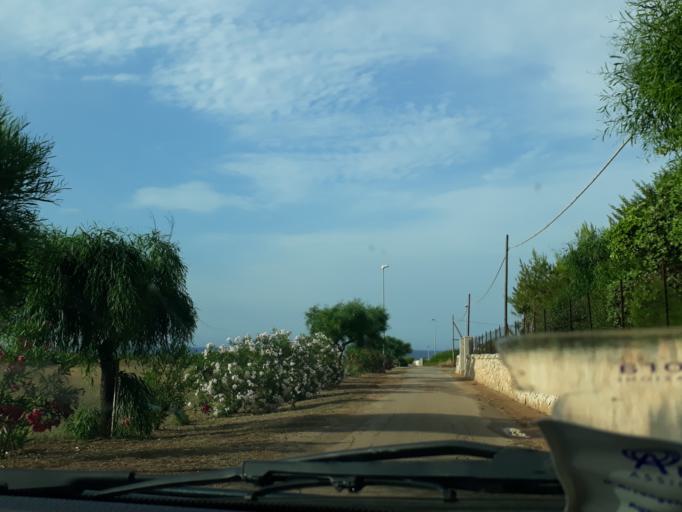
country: IT
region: Apulia
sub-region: Provincia di Brindisi
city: Carovigno
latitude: 40.7628
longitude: 17.6856
